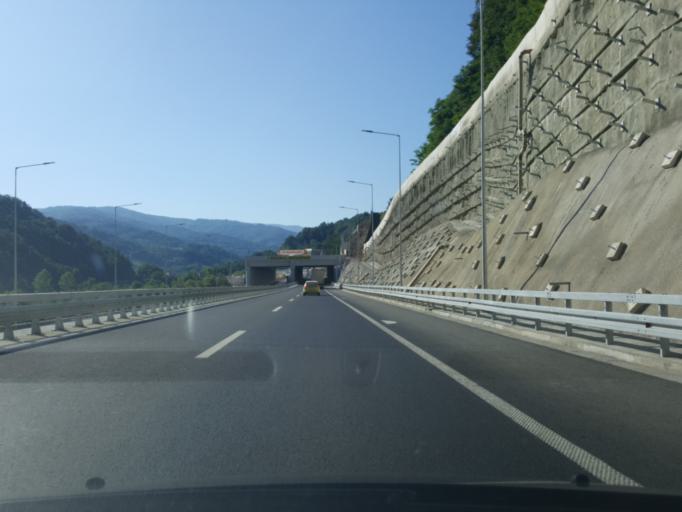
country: RS
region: Central Serbia
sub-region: Jablanicki Okrug
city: Vlasotince
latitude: 42.8701
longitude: 22.1024
